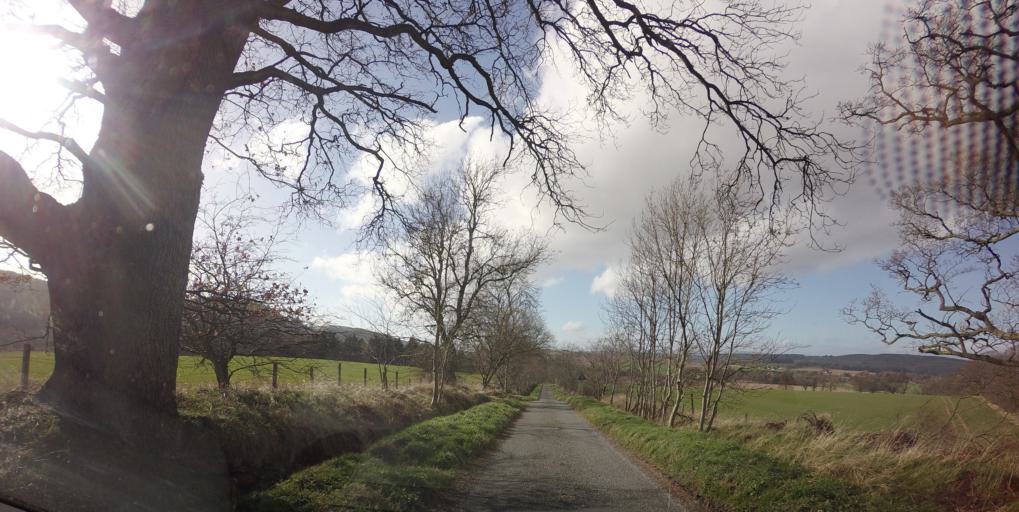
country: GB
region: Scotland
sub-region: Perth and Kinross
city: Bridge of Earn
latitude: 56.3292
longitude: -3.4167
